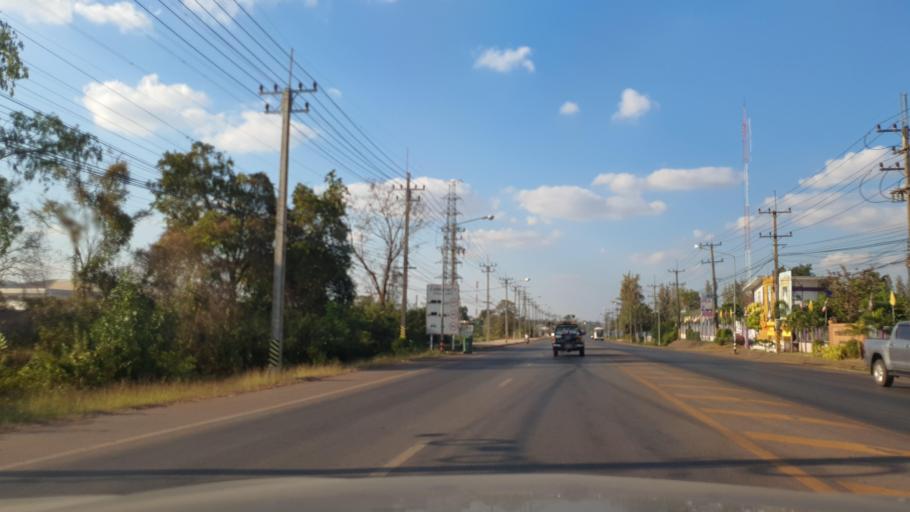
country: TH
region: Sakon Nakhon
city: Sakon Nakhon
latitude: 17.1449
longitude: 104.1093
